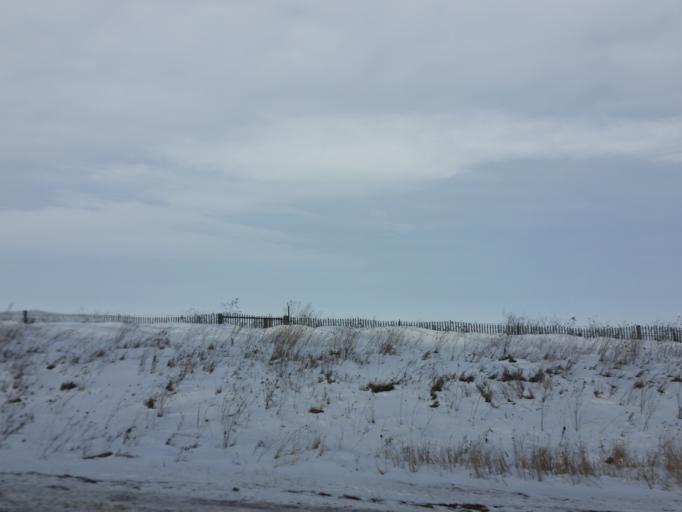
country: US
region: Iowa
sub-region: Delaware County
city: Manchester
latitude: 42.4642
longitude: -91.6397
